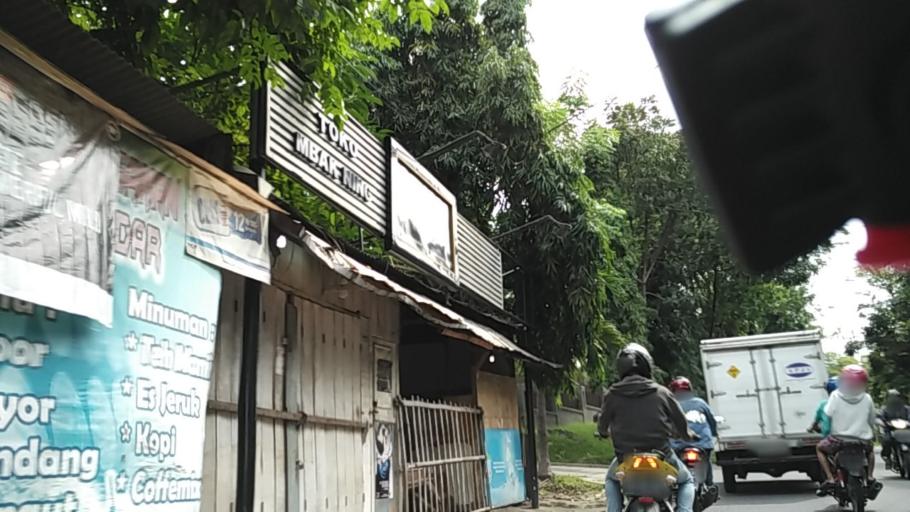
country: ID
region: Central Java
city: Semarang
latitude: -7.0027
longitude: 110.4103
